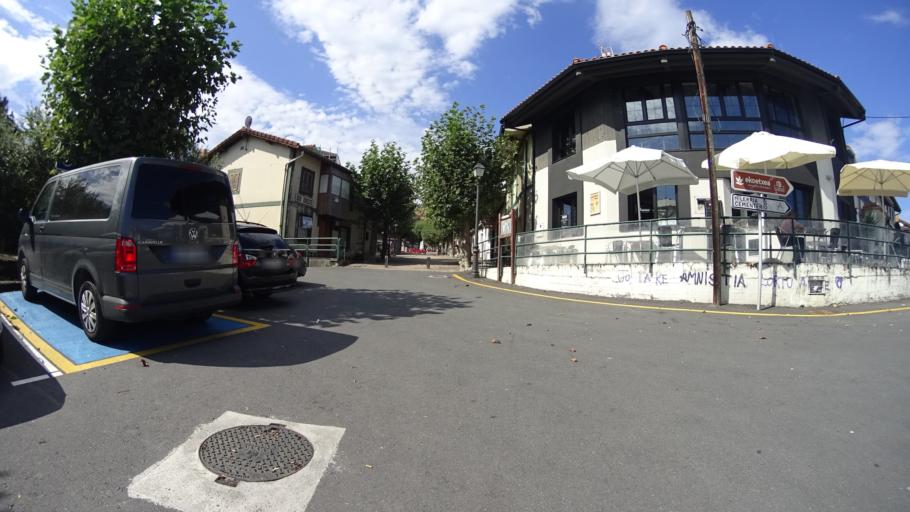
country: ES
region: Basque Country
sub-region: Bizkaia
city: Urtuella
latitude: 43.2846
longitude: -3.0543
